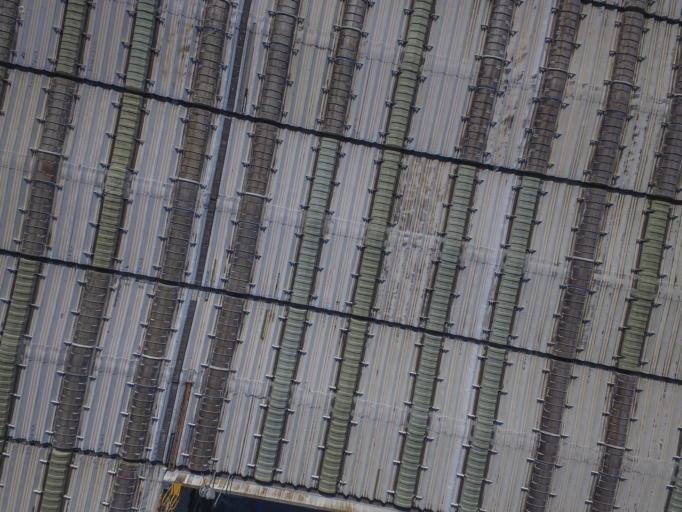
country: BR
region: Sao Paulo
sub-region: Jacarei
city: Jacarei
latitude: -23.2930
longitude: -45.9310
